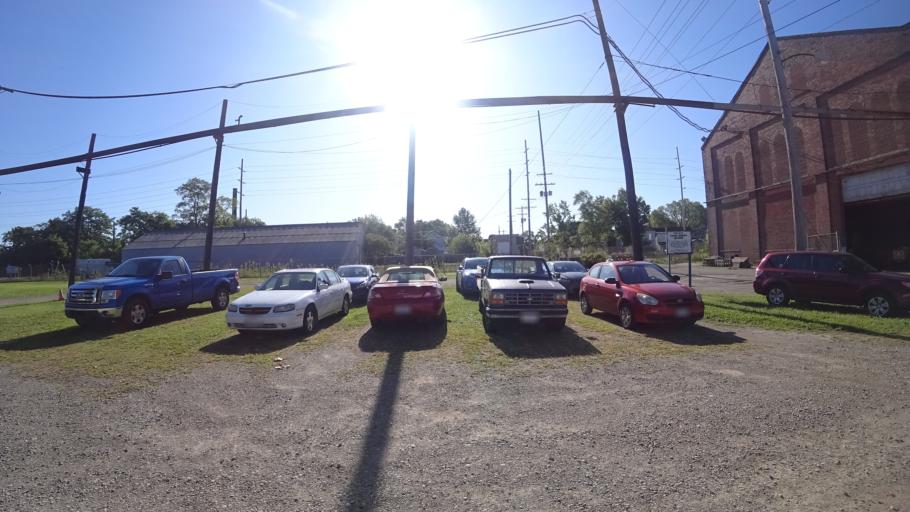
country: US
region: Ohio
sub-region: Butler County
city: Hamilton
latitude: 39.4048
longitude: -84.5555
